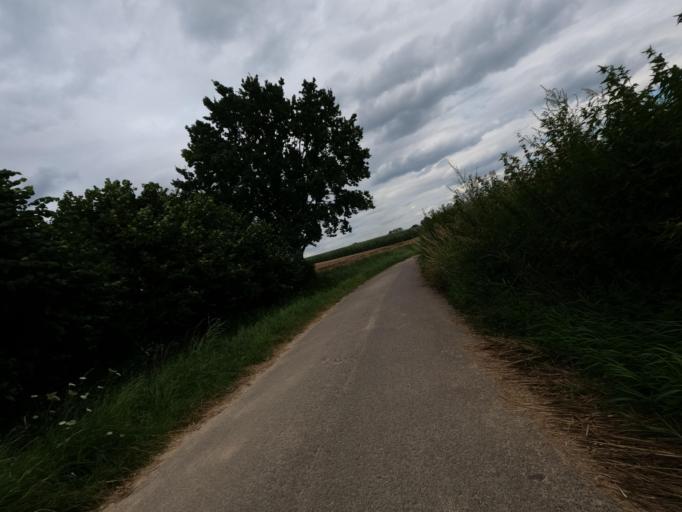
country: DE
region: North Rhine-Westphalia
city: Geilenkirchen
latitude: 50.9745
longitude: 6.1737
